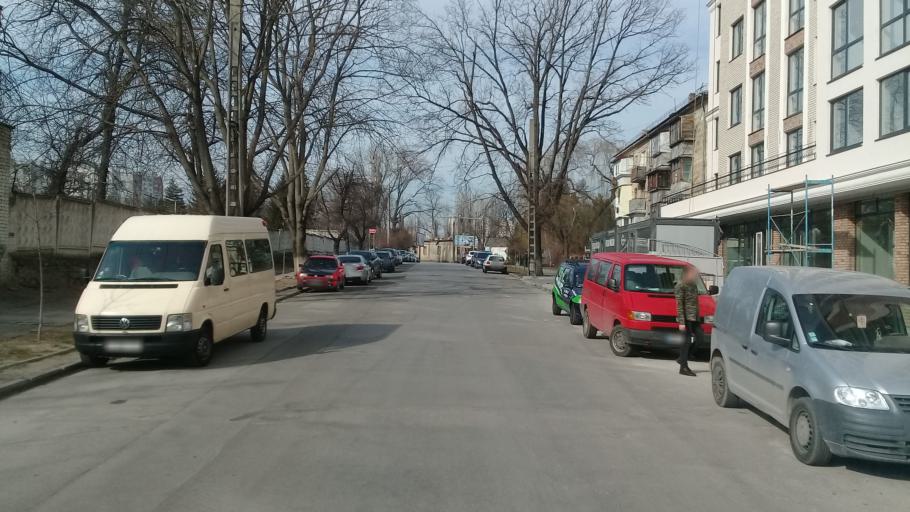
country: MD
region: Chisinau
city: Chisinau
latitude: 47.0208
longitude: 28.8059
